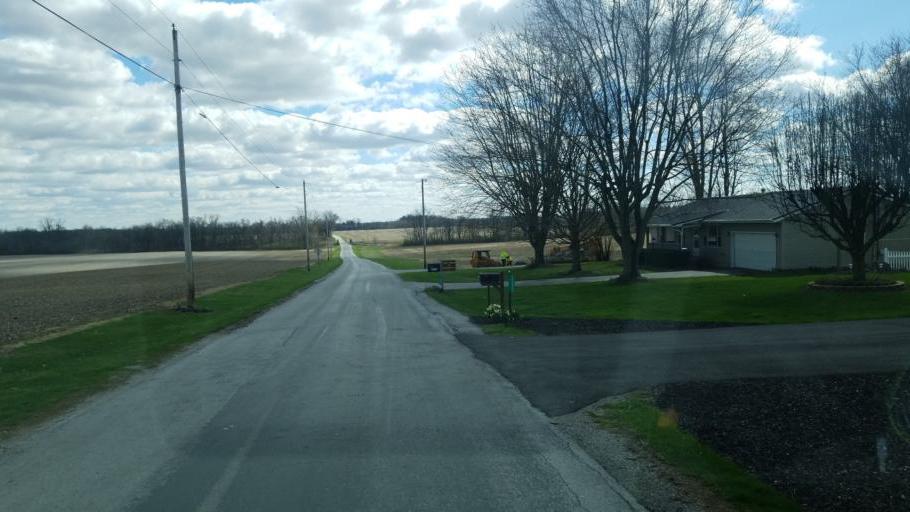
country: US
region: Ohio
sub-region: Hardin County
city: Kenton
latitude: 40.6375
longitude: -83.5619
